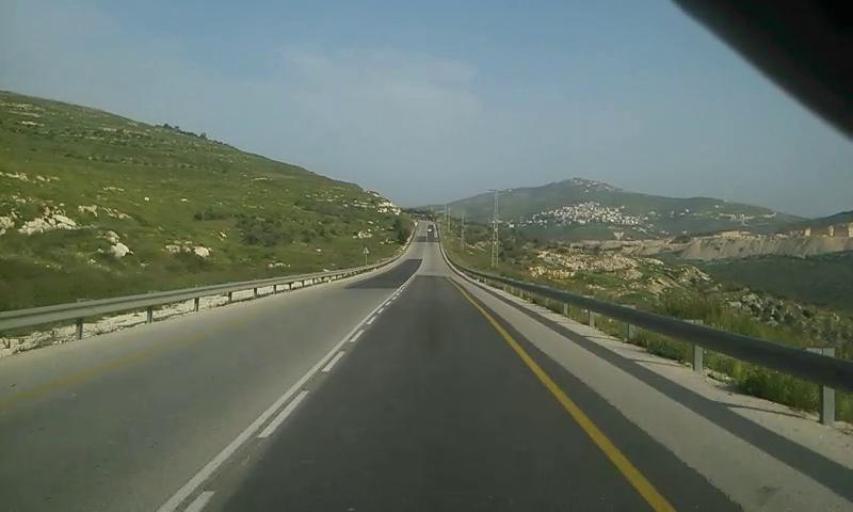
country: PS
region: West Bank
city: Sarrah
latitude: 32.1927
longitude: 35.1913
